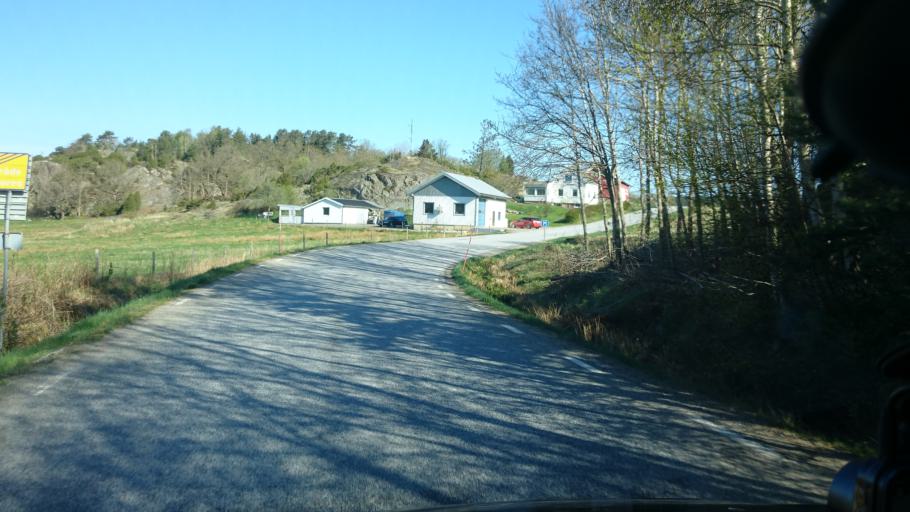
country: SE
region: Vaestra Goetaland
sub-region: Munkedals Kommun
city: Munkedal
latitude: 58.3844
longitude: 11.6629
